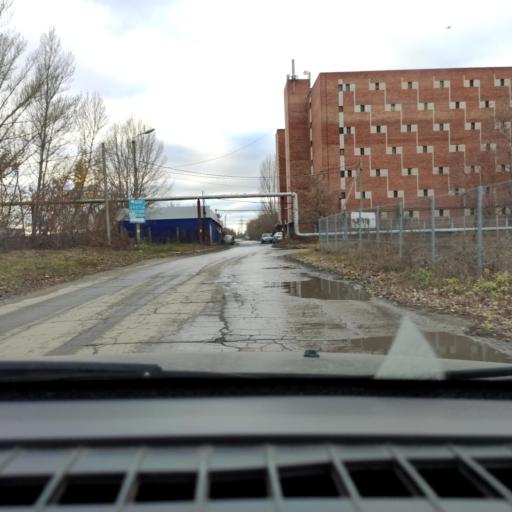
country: RU
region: Samara
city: Tol'yatti
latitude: 53.5447
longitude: 49.2925
